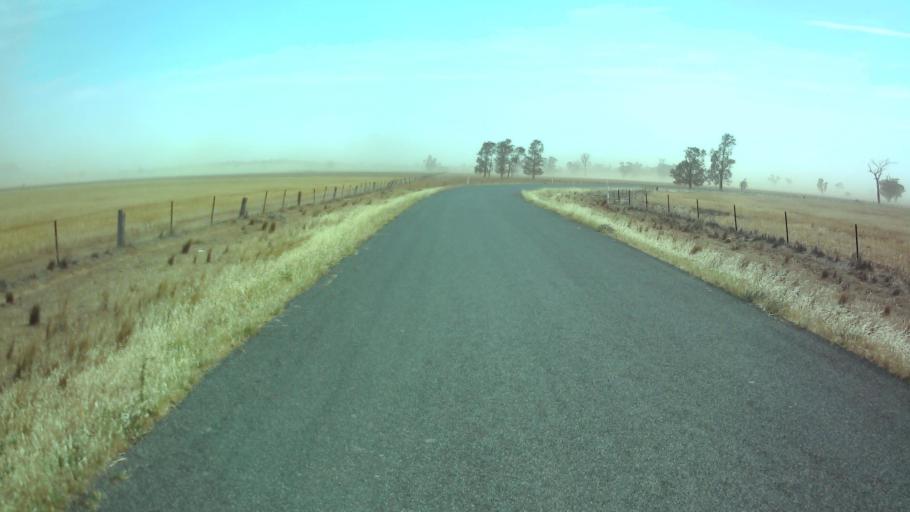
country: AU
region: New South Wales
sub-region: Weddin
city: Grenfell
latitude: -33.7388
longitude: 147.9930
